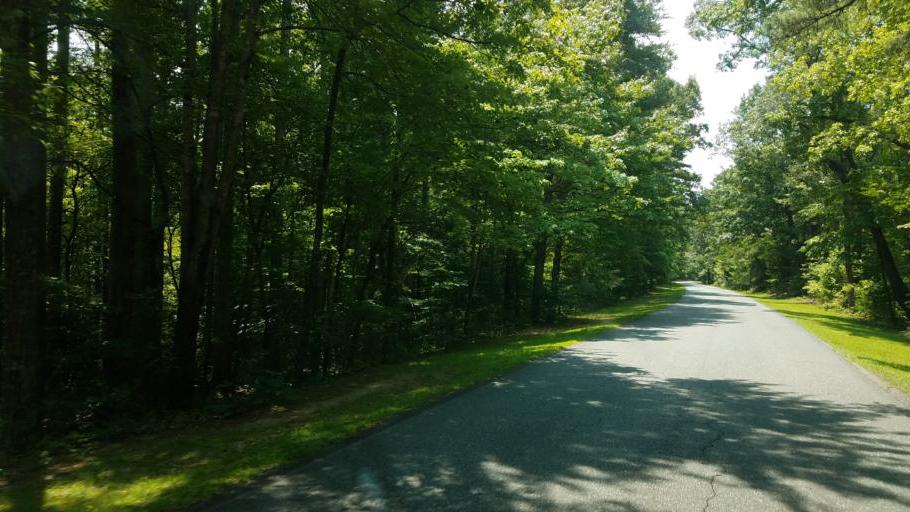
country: US
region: North Carolina
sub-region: Cleveland County
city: Kings Mountain
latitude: 35.1525
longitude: -81.3326
